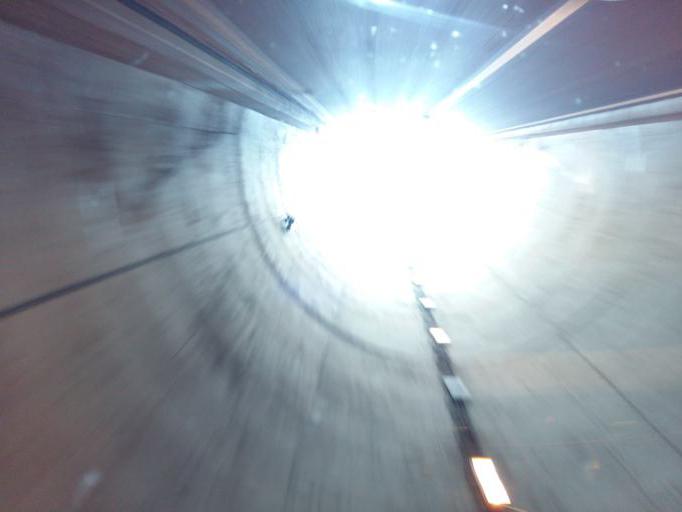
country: PT
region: Castelo Branco
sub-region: Concelho do Fundao
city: Fundao
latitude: 40.0969
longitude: -7.4715
